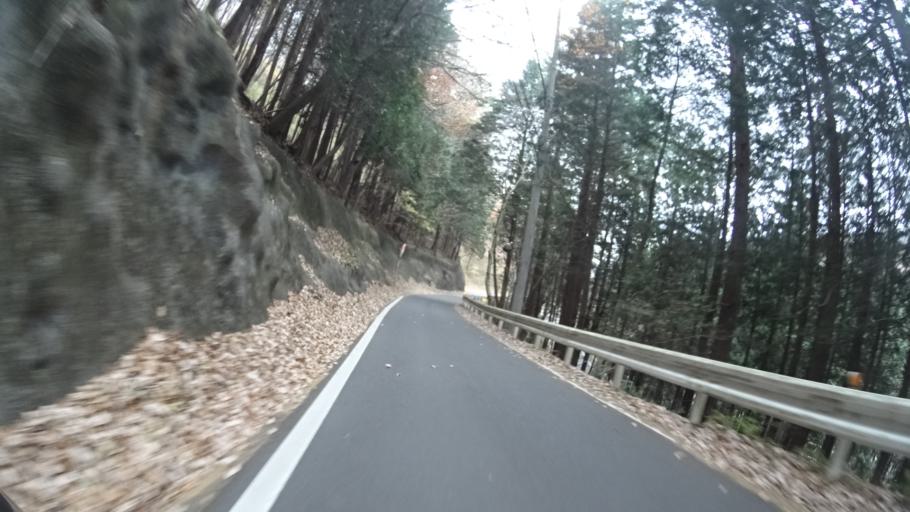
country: JP
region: Gunma
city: Omamacho-omama
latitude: 36.4922
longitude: 139.1853
